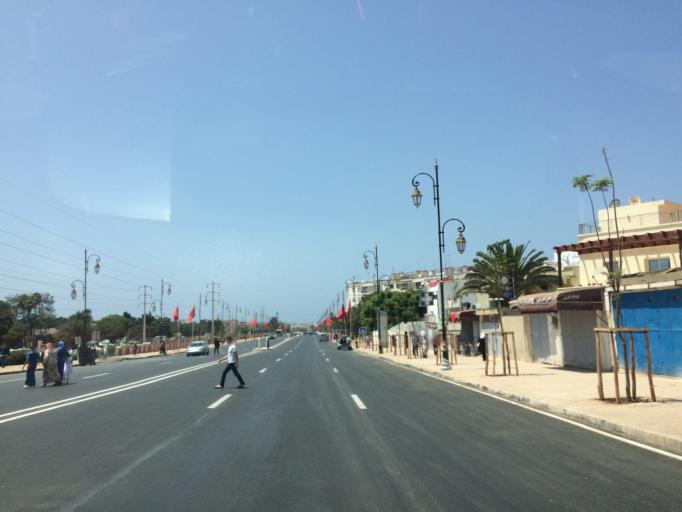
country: MA
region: Rabat-Sale-Zemmour-Zaer
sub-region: Rabat
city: Rabat
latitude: 33.9874
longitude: -6.8527
